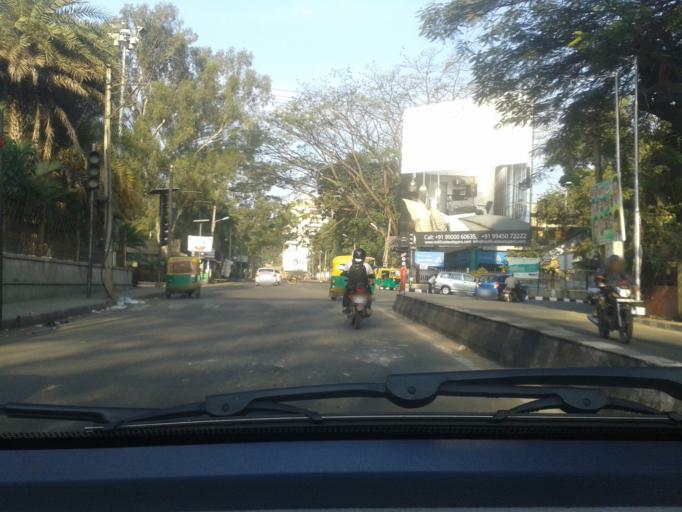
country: IN
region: Karnataka
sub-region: Bangalore Urban
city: Bangalore
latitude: 12.9953
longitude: 77.6023
